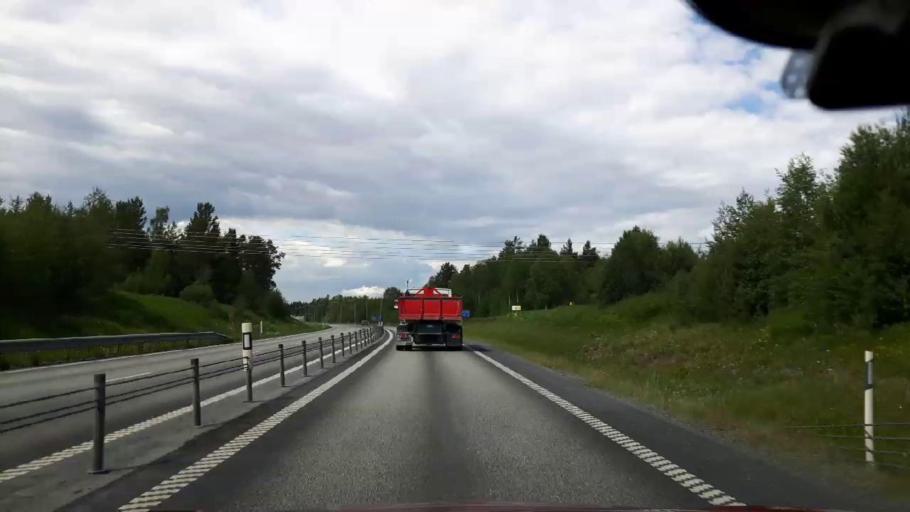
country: SE
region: Jaemtland
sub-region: OEstersunds Kommun
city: Ostersund
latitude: 63.2119
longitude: 14.6601
